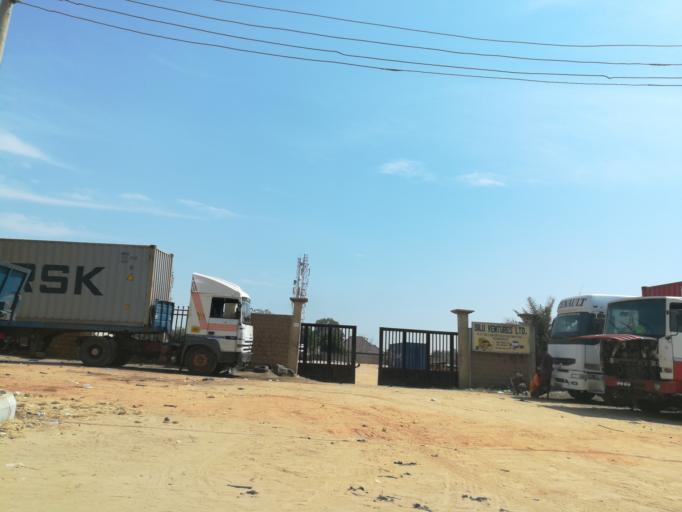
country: NG
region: Kano
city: Kano
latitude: 12.0294
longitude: 8.5155
